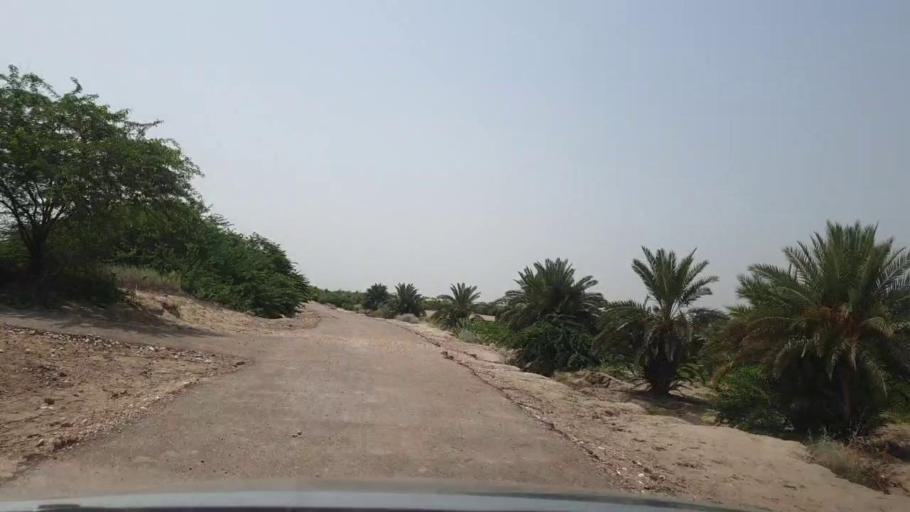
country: PK
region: Sindh
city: Pano Aqil
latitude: 27.6095
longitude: 69.1460
